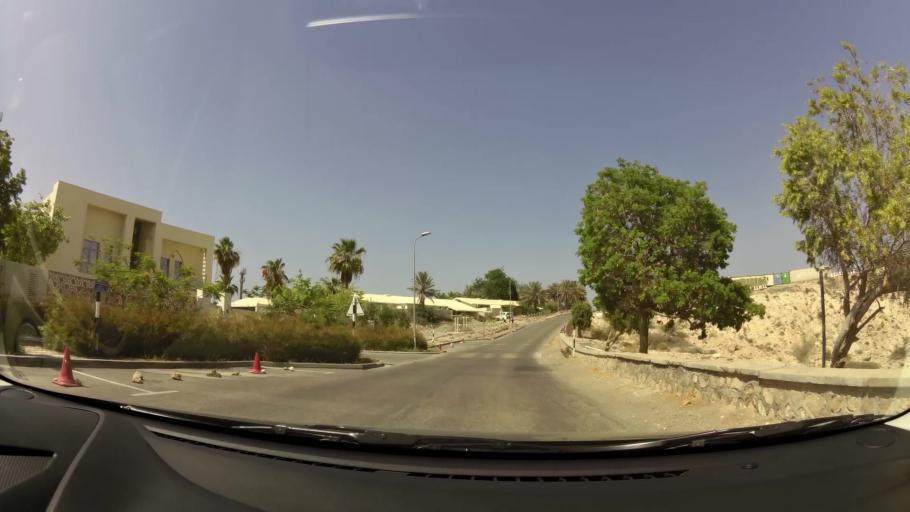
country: OM
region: Muhafazat Masqat
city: Muscat
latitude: 23.6377
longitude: 58.4952
